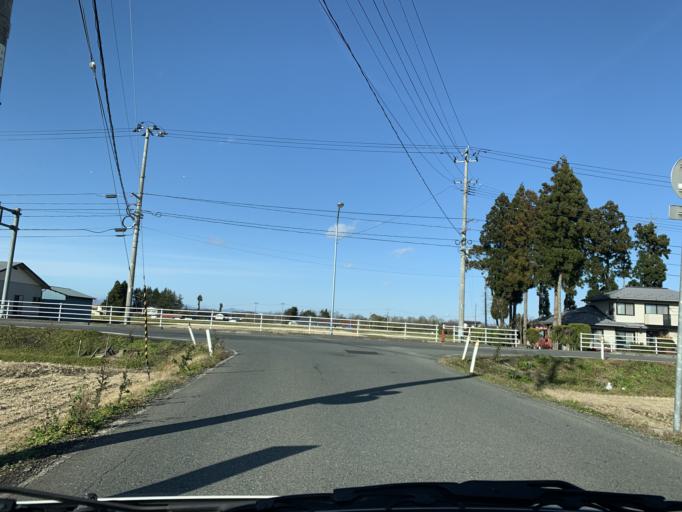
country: JP
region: Iwate
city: Mizusawa
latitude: 39.1635
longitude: 141.0988
